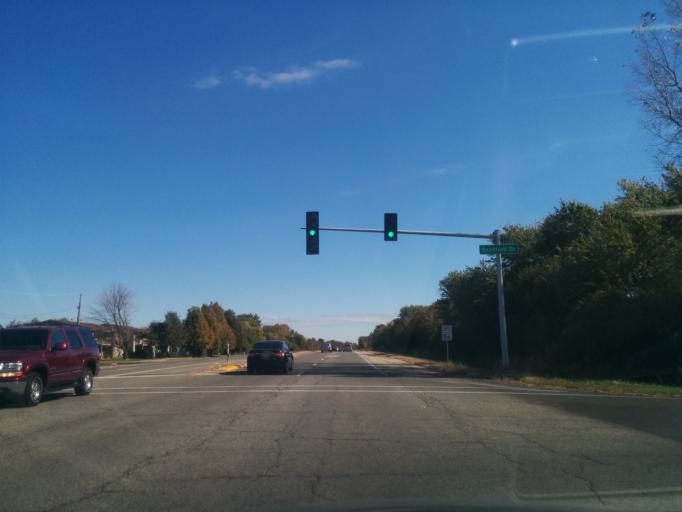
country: US
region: Illinois
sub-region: DuPage County
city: Lisle
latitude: 41.8295
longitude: -88.0895
